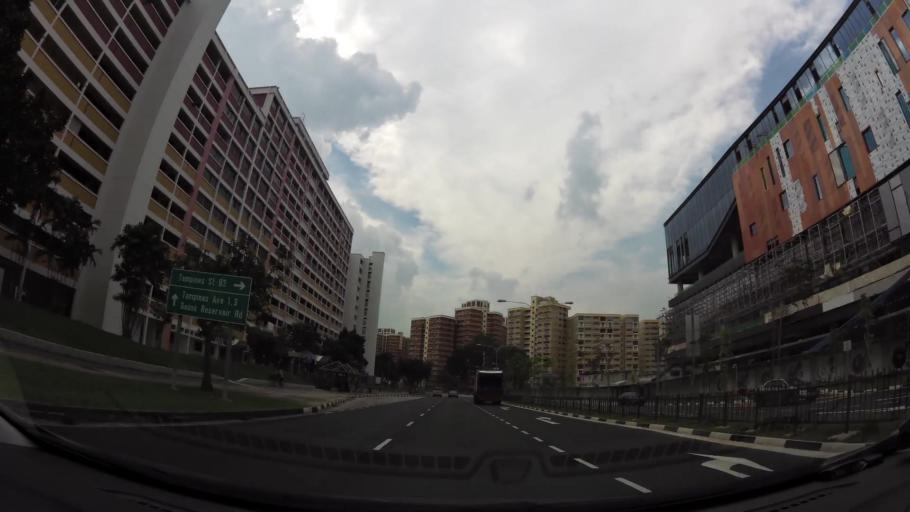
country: SG
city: Singapore
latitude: 1.3518
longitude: 103.9406
